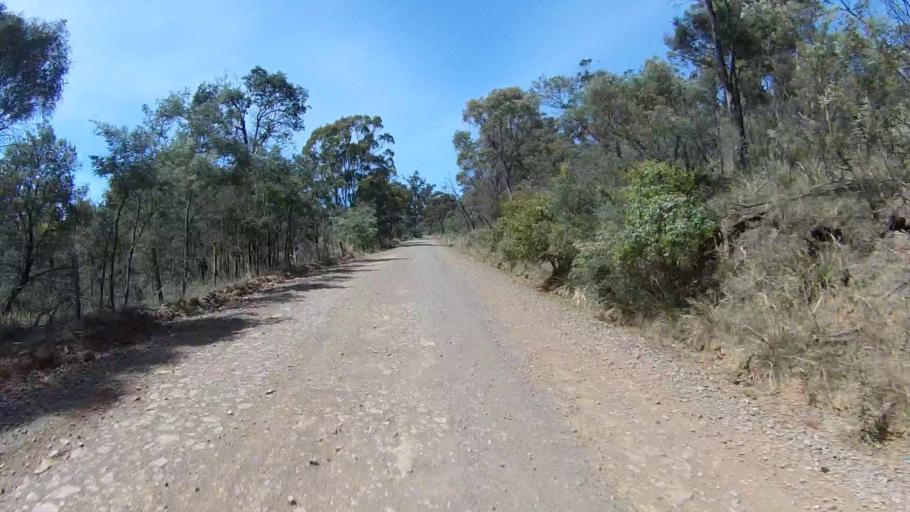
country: AU
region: Tasmania
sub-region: Sorell
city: Sorell
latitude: -42.6466
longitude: 147.7423
